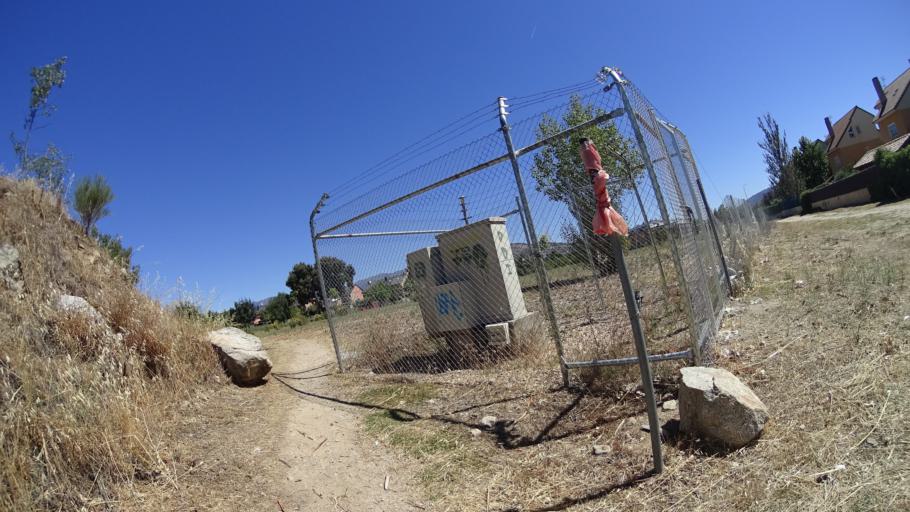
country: ES
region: Madrid
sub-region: Provincia de Madrid
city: Alpedrete
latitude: 40.6440
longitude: -4.0248
